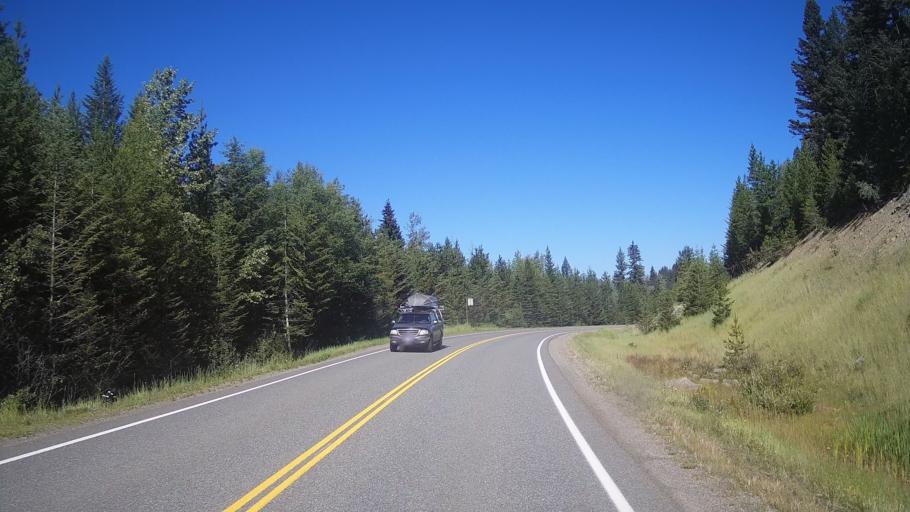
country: CA
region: British Columbia
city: Kamloops
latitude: 51.4726
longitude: -120.5525
